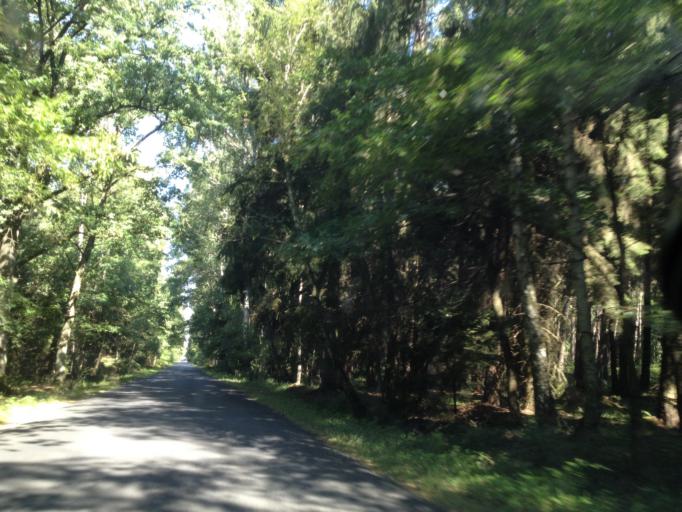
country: PL
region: Greater Poland Voivodeship
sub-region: Powiat sredzki
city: Zaniemysl
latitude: 52.1285
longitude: 17.1053
